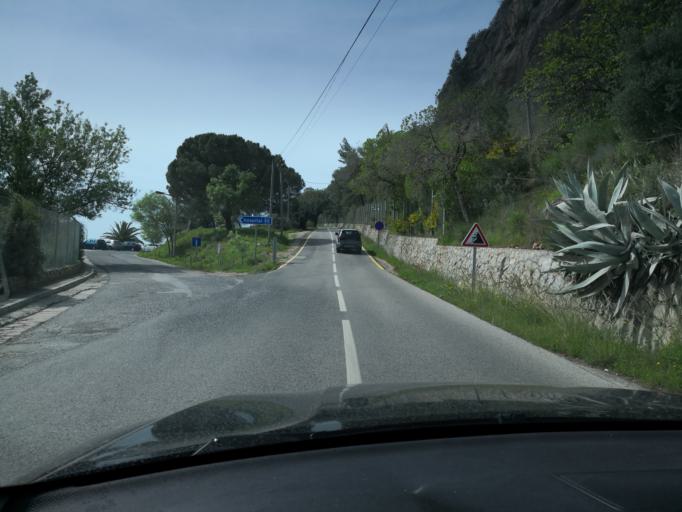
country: PT
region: Setubal
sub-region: Setubal
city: Setubal
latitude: 38.4919
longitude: -8.9345
